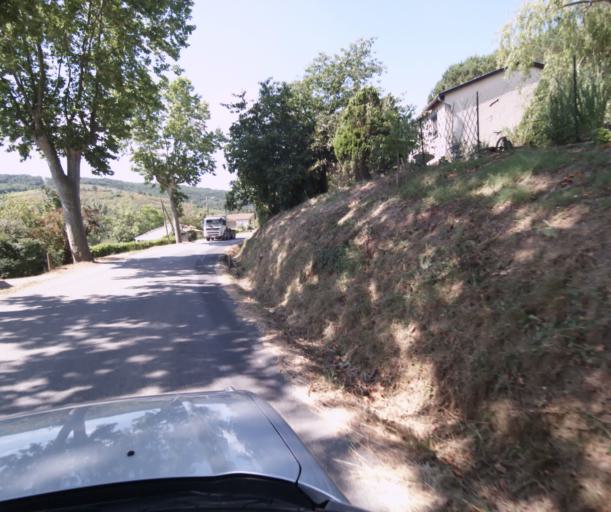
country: FR
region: Languedoc-Roussillon
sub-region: Departement de l'Aude
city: Limoux
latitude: 43.0452
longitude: 2.2213
